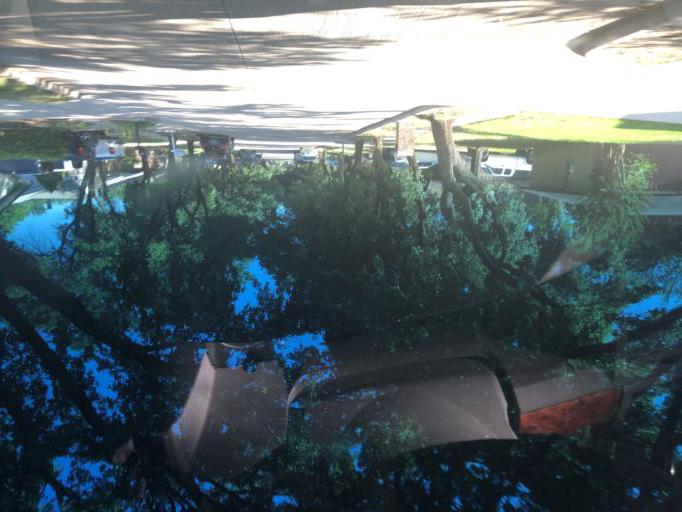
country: US
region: Texas
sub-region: Dallas County
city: Grand Prairie
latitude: 32.7067
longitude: -97.0019
